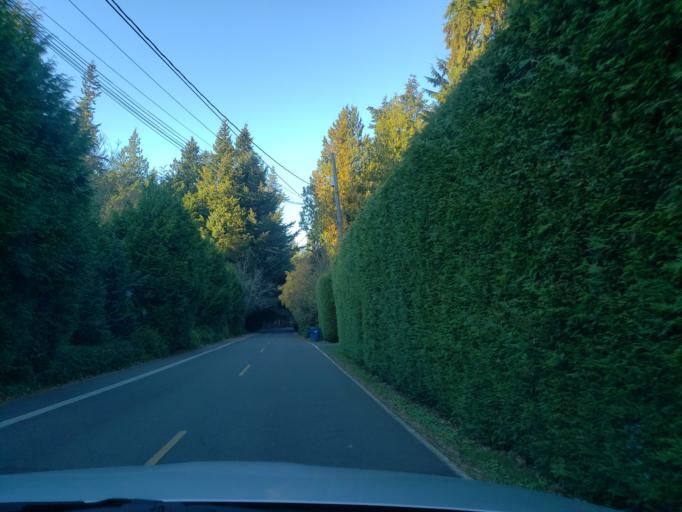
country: US
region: Washington
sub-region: Snohomish County
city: Woodway
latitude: 47.7854
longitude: -122.3830
